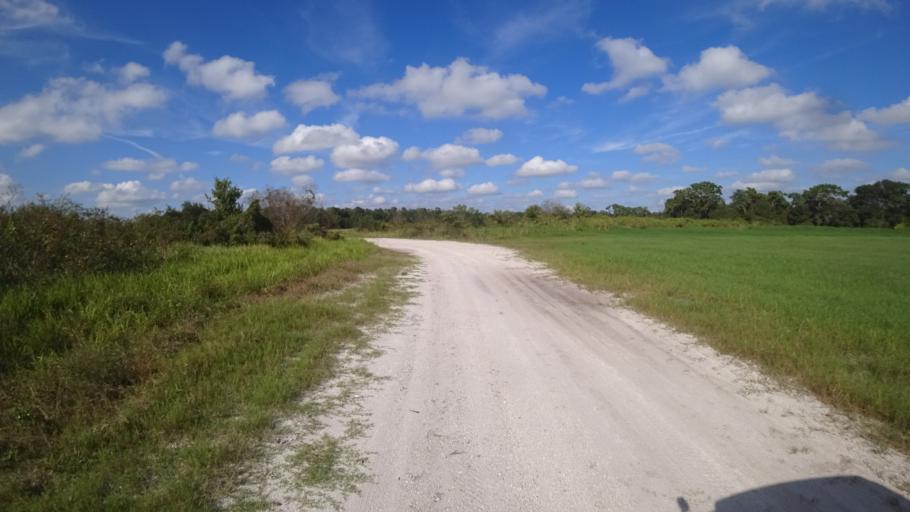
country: US
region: Florida
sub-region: Sarasota County
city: Lake Sarasota
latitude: 27.3720
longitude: -82.1574
